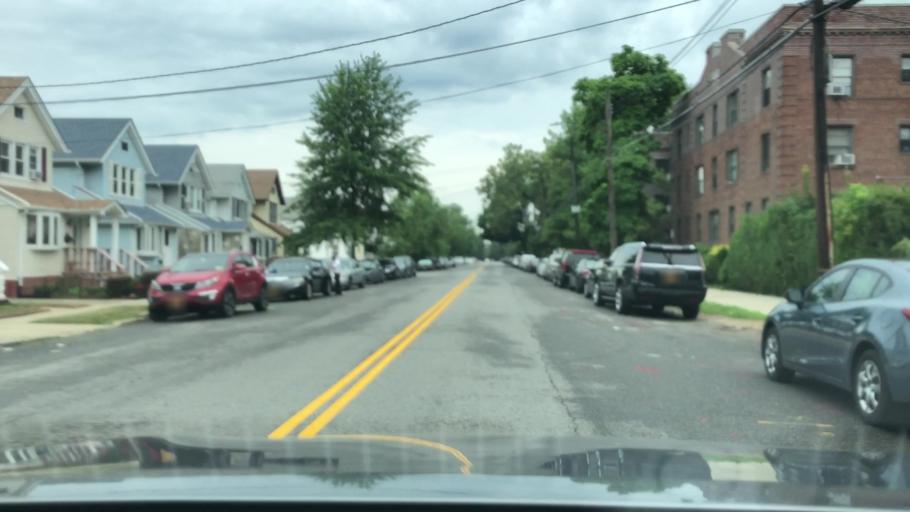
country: US
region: New York
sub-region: Nassau County
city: Bellerose Terrace
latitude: 40.7212
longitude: -73.7328
